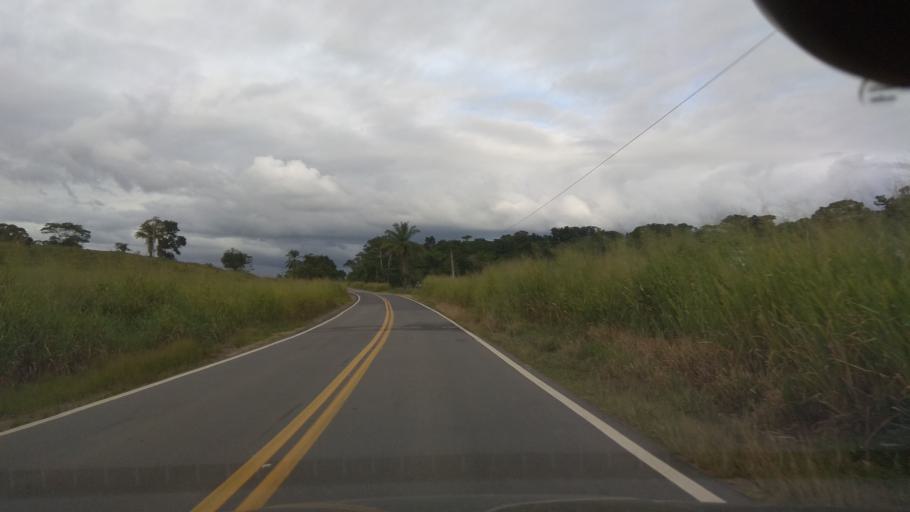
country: BR
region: Bahia
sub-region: Ipiau
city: Ipiau
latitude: -14.1935
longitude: -39.6504
